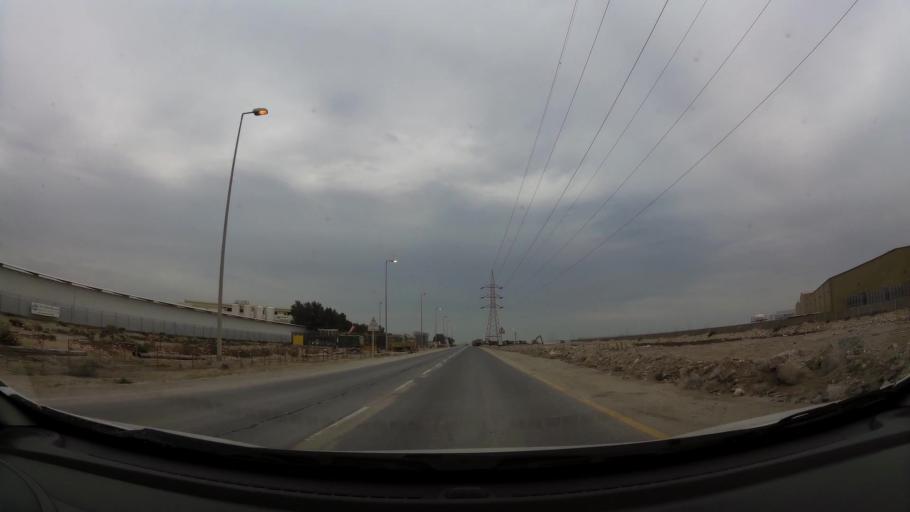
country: BH
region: Northern
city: Sitrah
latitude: 26.1785
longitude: 50.6212
